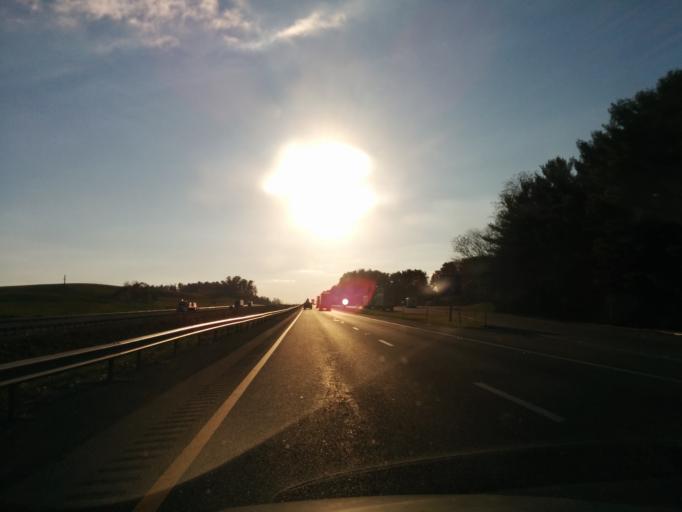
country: US
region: Virginia
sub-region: Rockbridge County
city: East Lexington
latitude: 37.8762
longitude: -79.3068
